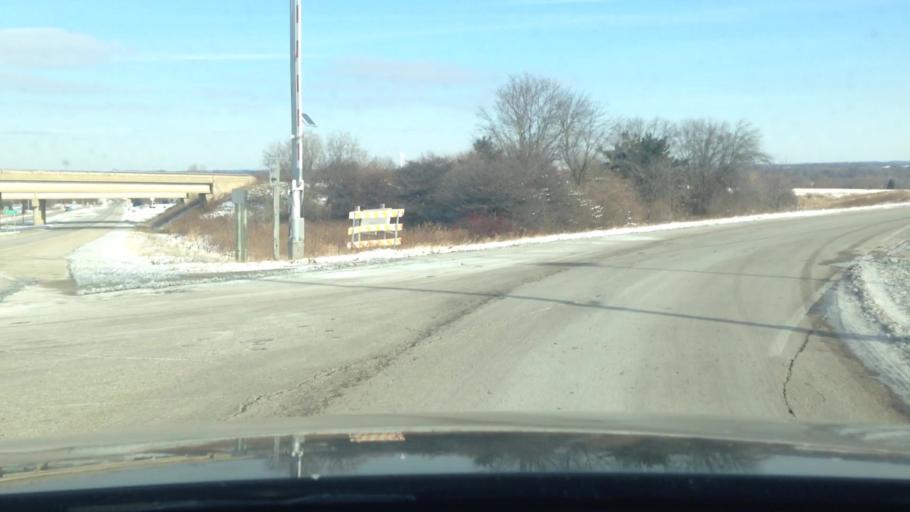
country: US
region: Wisconsin
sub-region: Walworth County
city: East Troy
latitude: 42.7725
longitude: -88.4057
